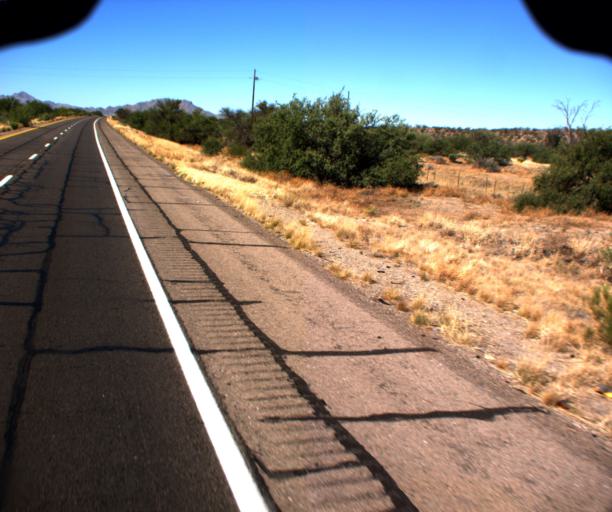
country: US
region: Arizona
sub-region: Pima County
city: Arivaca Junction
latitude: 31.7433
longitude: -111.0479
